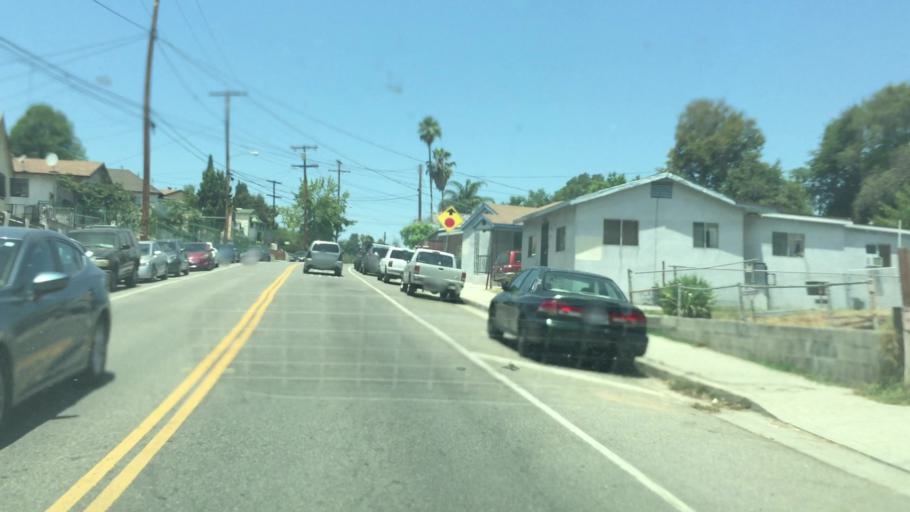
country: US
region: California
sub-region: Los Angeles County
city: Glendale
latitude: 34.1142
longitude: -118.2090
